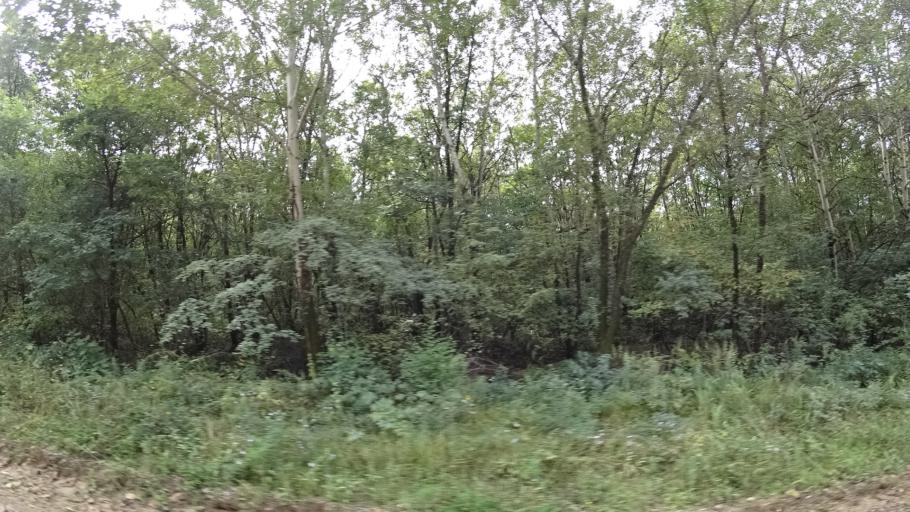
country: RU
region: Primorskiy
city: Lyalichi
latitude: 44.0962
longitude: 132.4304
